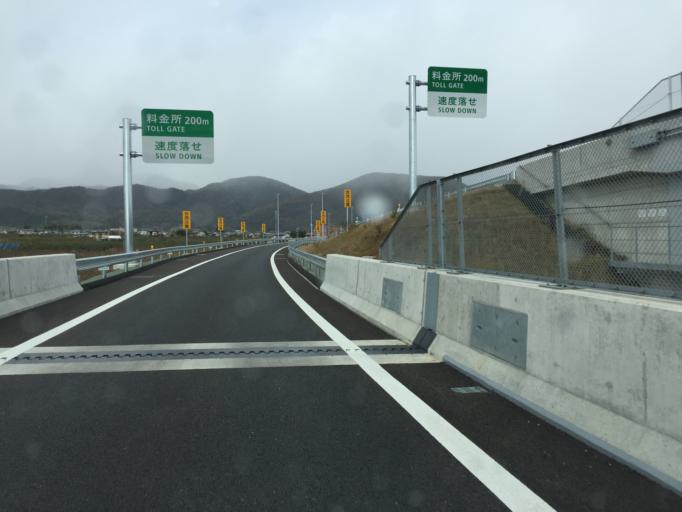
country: JP
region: Fukushima
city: Fukushima-shi
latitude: 37.7897
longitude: 140.4160
